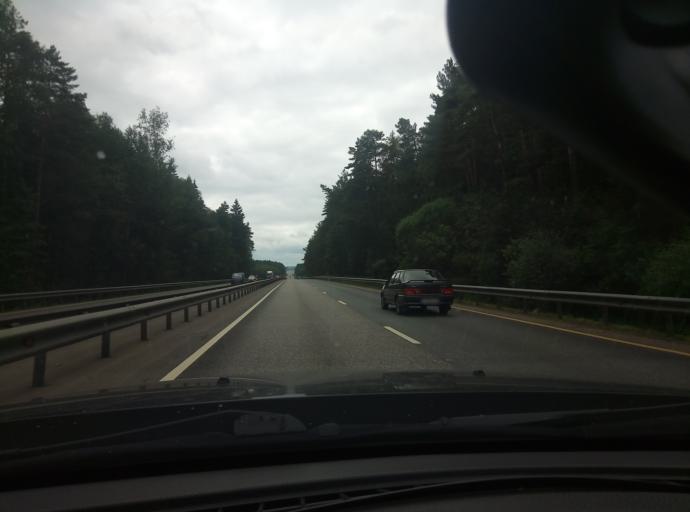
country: RU
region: Kaluga
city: Maloyaroslavets
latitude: 54.9717
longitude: 36.4808
